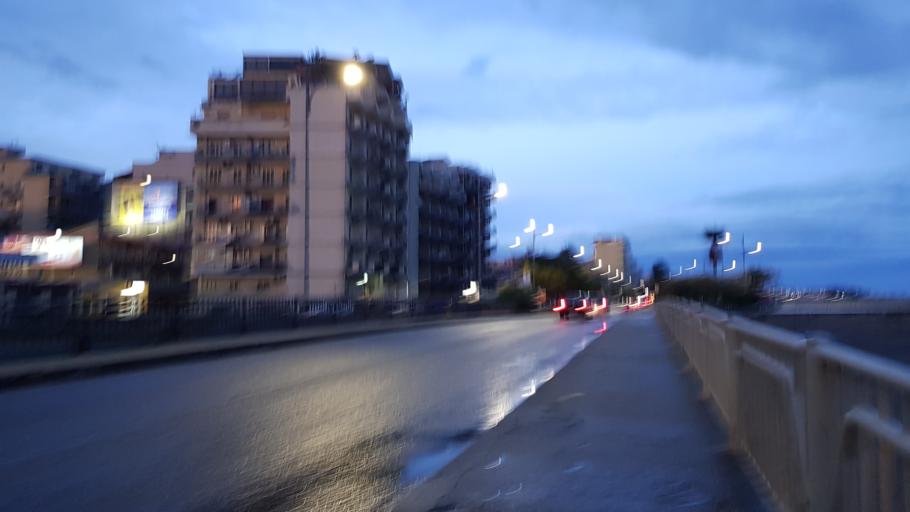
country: IT
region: Calabria
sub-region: Provincia di Catanzaro
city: Roccelletta
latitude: 38.8224
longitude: 16.6187
